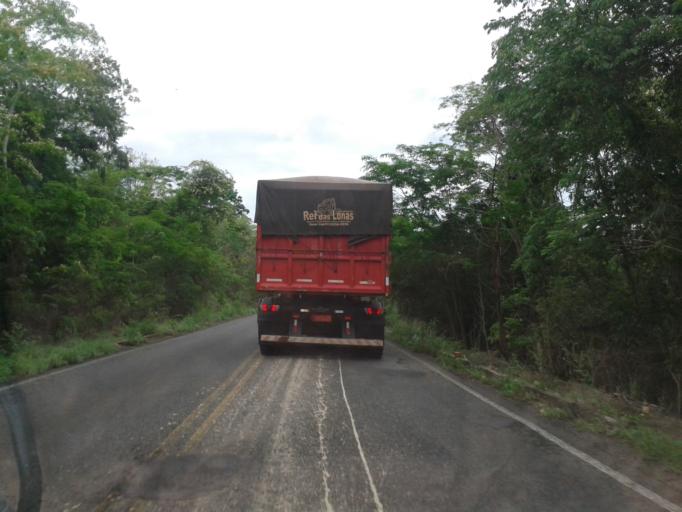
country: BR
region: Goias
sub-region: Caldas Novas
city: Caldas Novas
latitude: -18.0633
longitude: -48.6804
